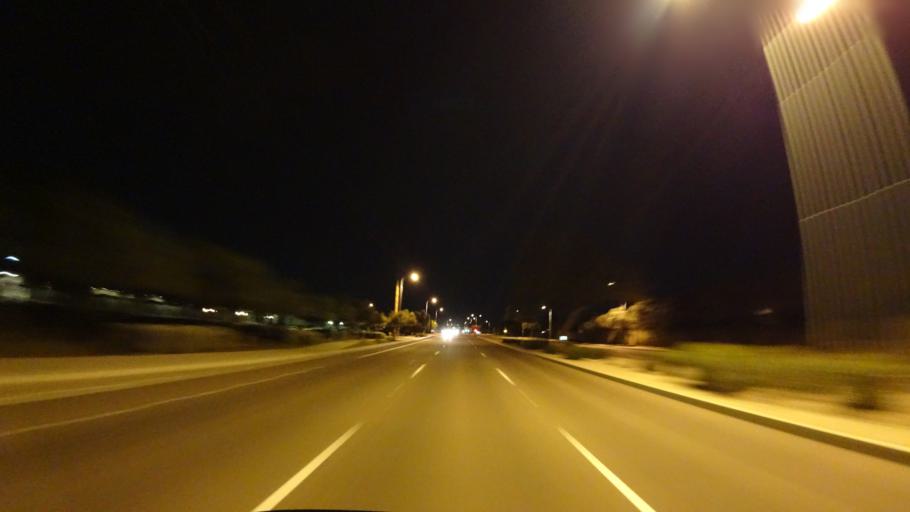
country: US
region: Arizona
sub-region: Maricopa County
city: San Carlos
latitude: 33.3206
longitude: -111.8821
